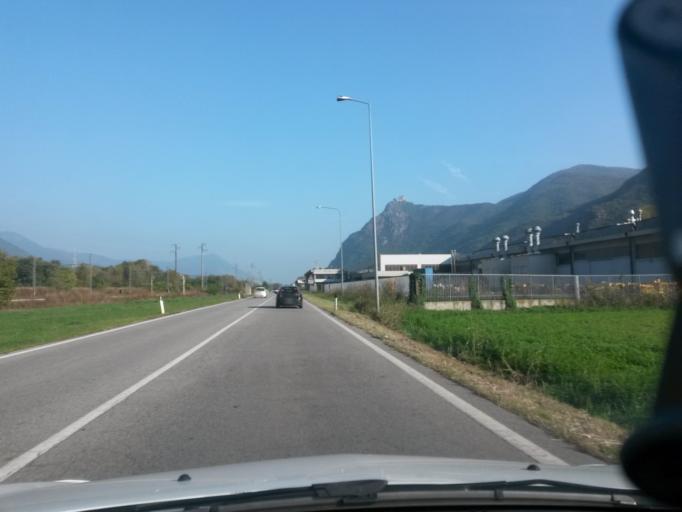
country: IT
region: Piedmont
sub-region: Provincia di Torino
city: Vaie
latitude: 45.1071
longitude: 7.2984
